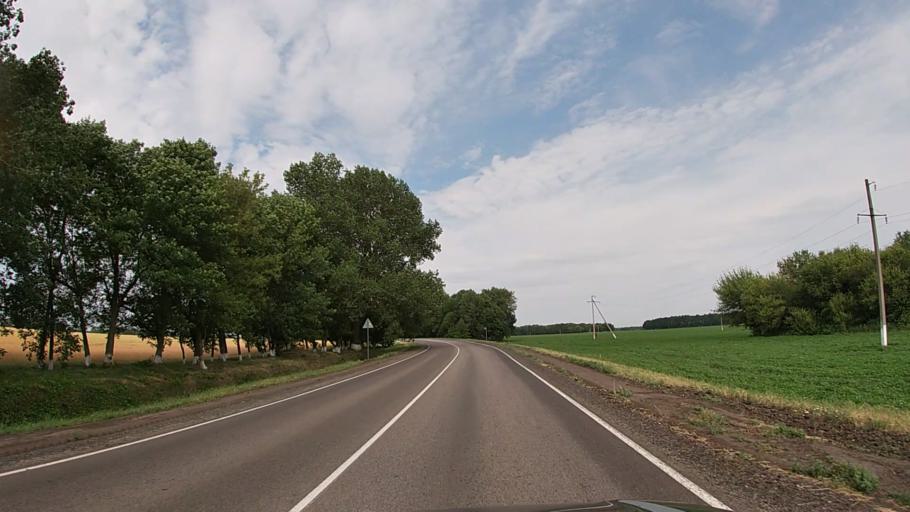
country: RU
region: Belgorod
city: Krasnaya Yaruga
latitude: 50.8107
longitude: 35.5120
